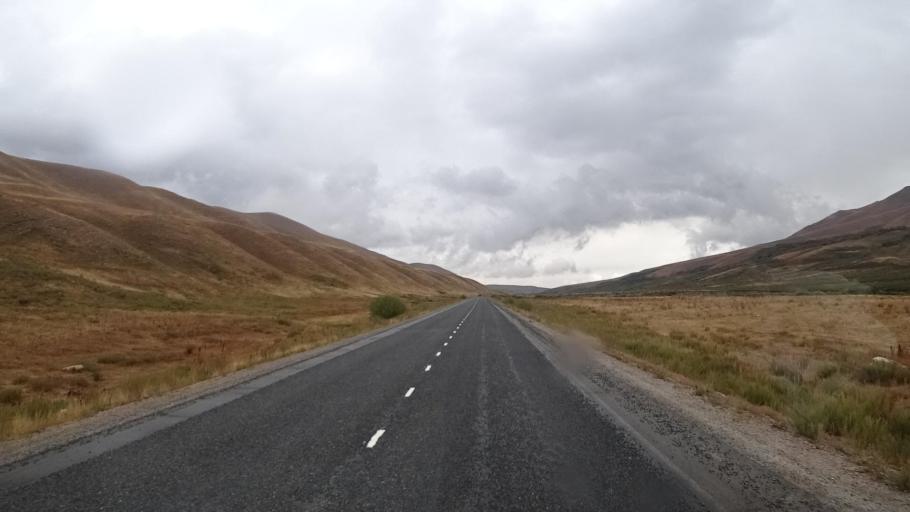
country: KG
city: Sosnovka
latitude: 42.1995
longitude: 73.5782
